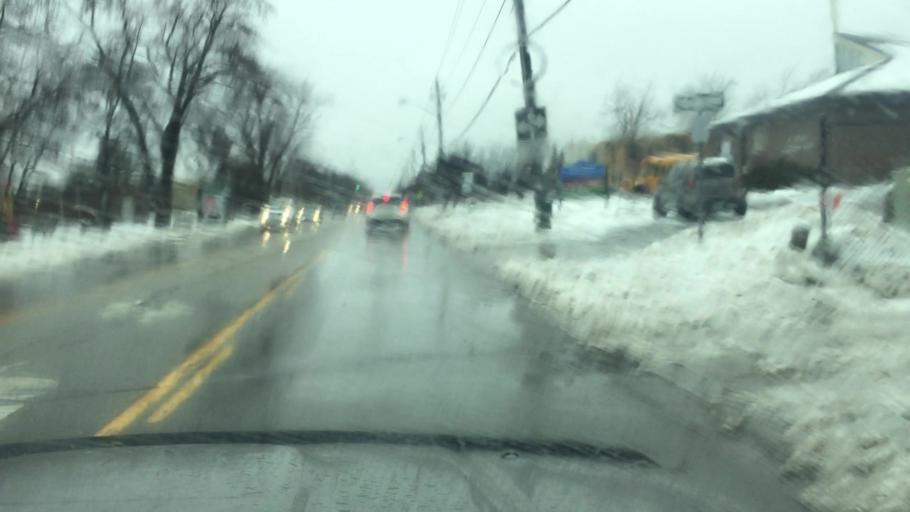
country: CA
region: Ontario
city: Ajax
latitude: 43.8561
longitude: -79.0563
